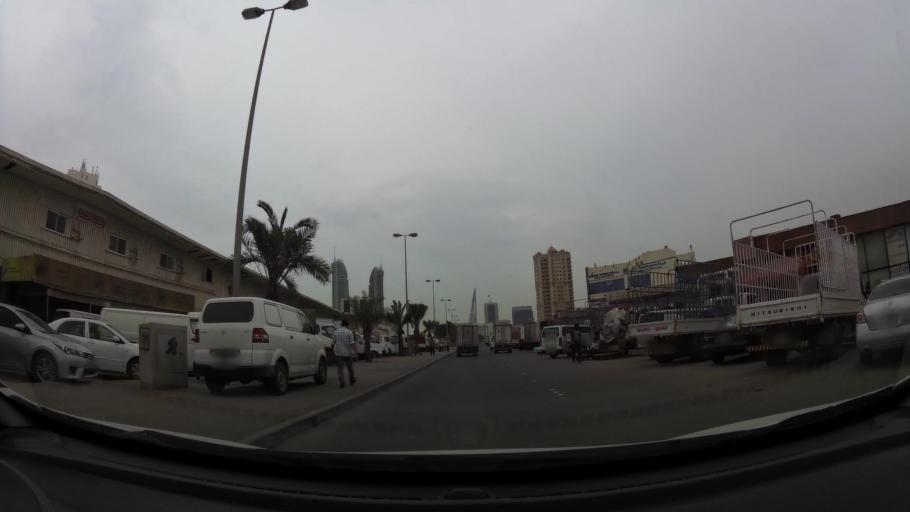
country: BH
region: Manama
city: Jidd Hafs
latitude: 26.2293
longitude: 50.5657
